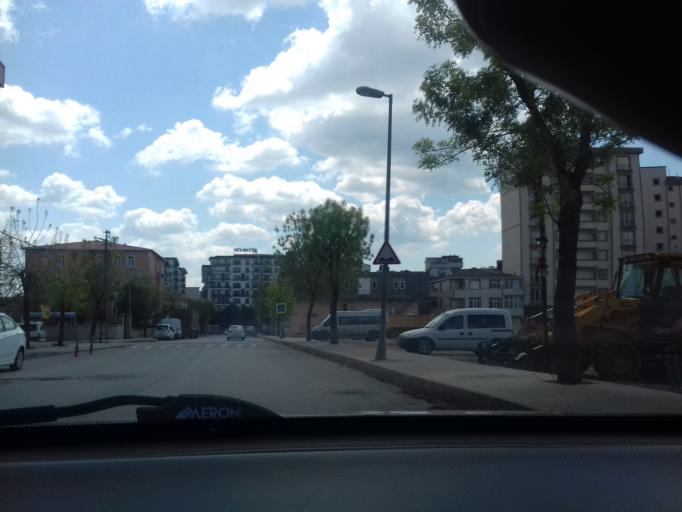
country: TR
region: Istanbul
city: Pendik
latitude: 40.8942
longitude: 29.2756
